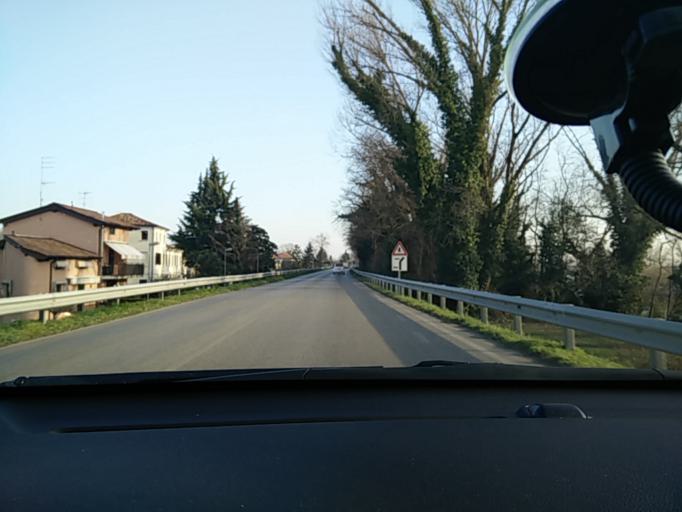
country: IT
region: Veneto
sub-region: Provincia di Venezia
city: San Dona di Piave
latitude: 45.6251
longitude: 12.5700
